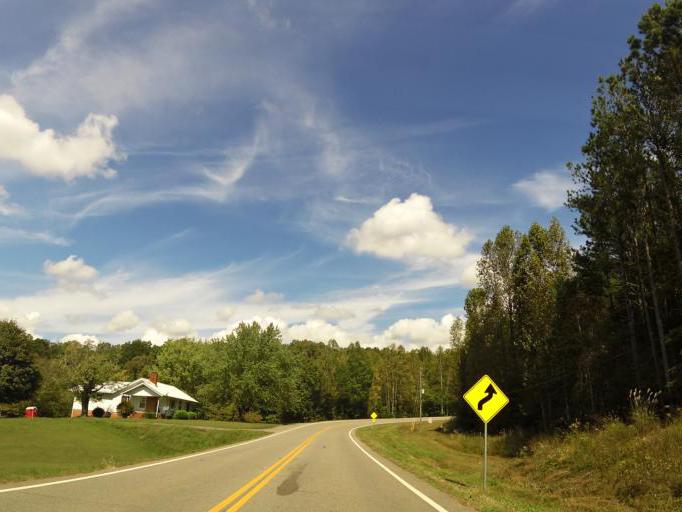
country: US
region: Georgia
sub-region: Pickens County
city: Jasper
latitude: 34.5485
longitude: -84.2604
